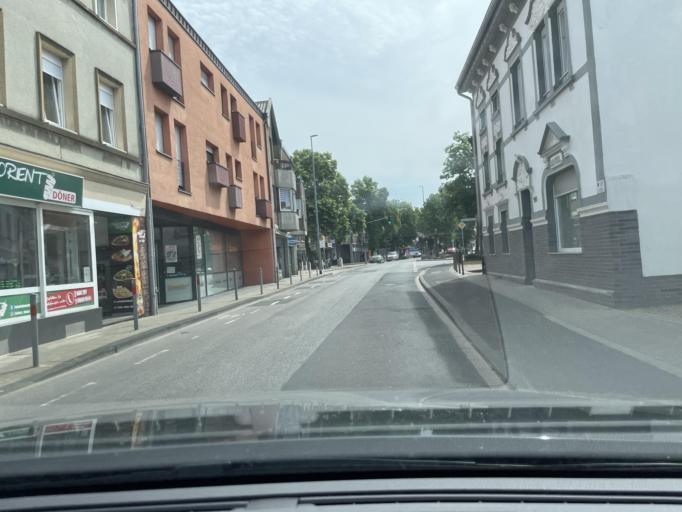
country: DE
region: North Rhine-Westphalia
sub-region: Regierungsbezirk Dusseldorf
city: Viersen
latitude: 51.2061
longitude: 6.3410
